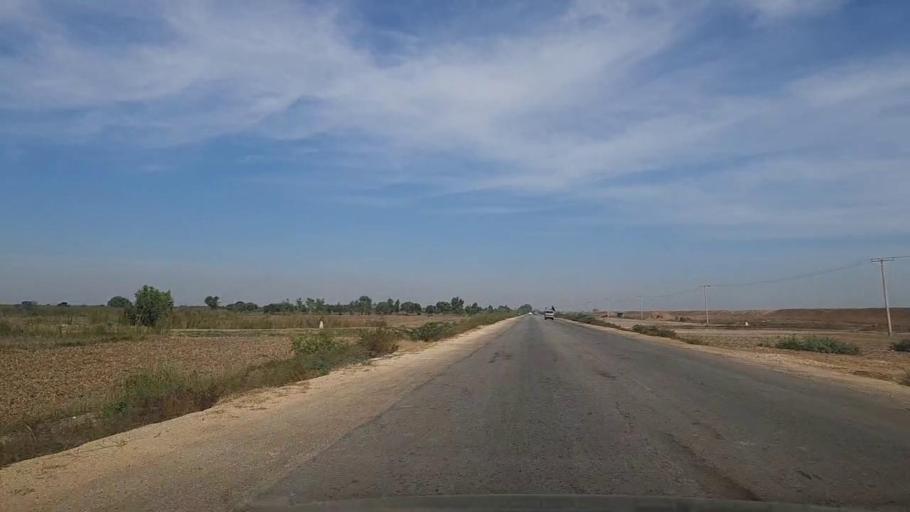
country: PK
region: Sindh
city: Daro Mehar
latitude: 24.9472
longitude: 68.1118
